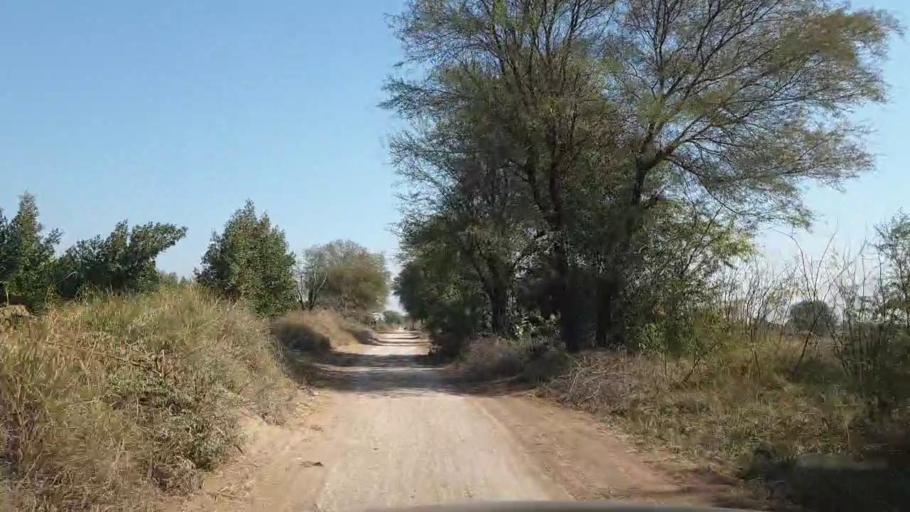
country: PK
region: Sindh
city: Tando Adam
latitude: 25.6402
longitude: 68.6991
